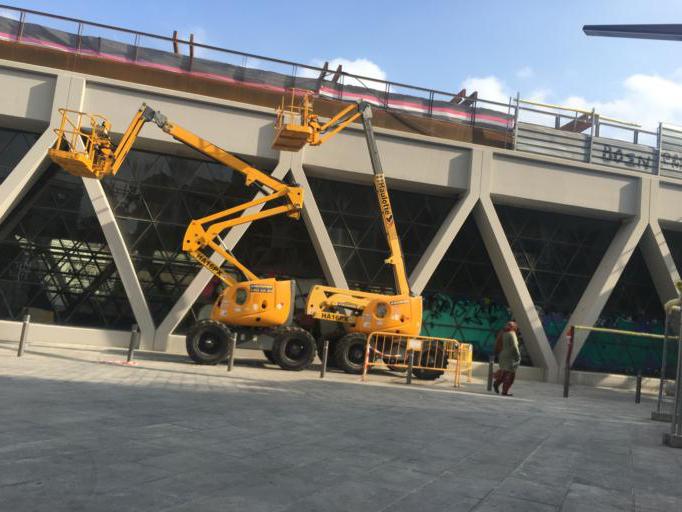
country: ES
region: Catalonia
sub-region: Provincia de Barcelona
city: les Corts
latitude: 41.3719
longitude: 2.1317
